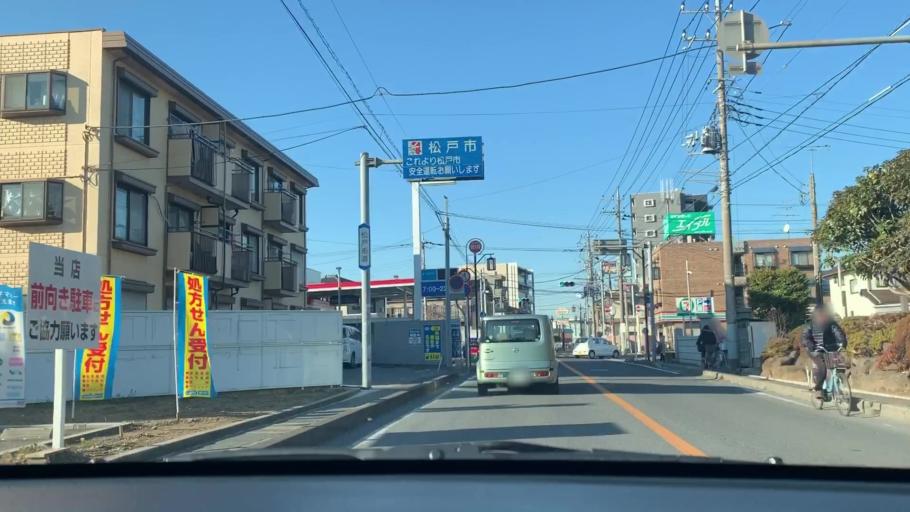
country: JP
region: Chiba
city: Matsudo
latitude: 35.7542
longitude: 139.9003
